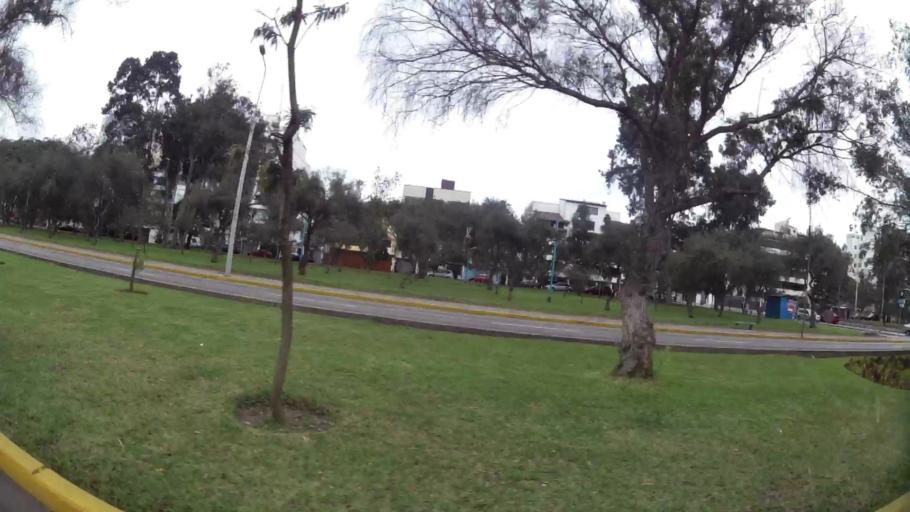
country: PE
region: Lima
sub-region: Lima
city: San Luis
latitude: -12.1013
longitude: -76.9924
